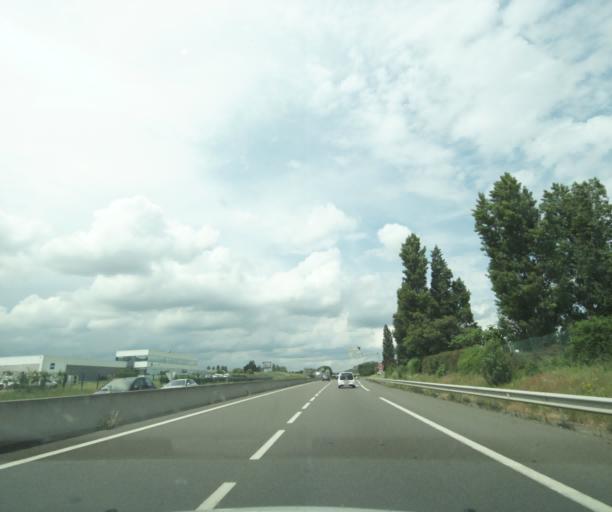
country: FR
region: Auvergne
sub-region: Departement du Puy-de-Dome
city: Perignat-les-Sarlieve
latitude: 45.7552
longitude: 3.1415
